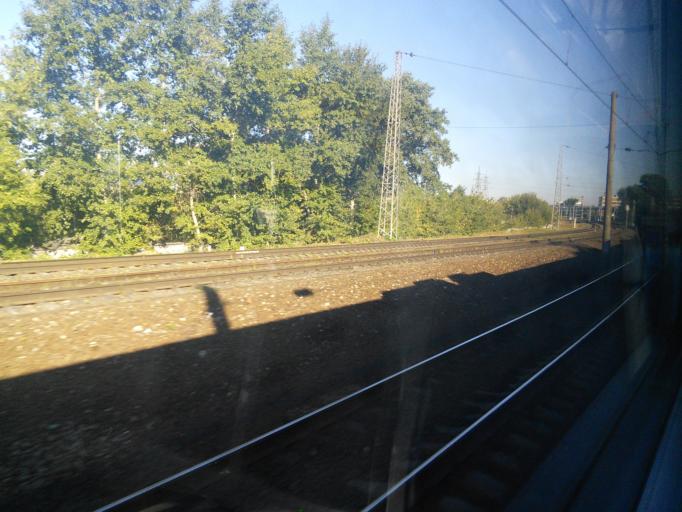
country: RU
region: Moscow
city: Tekstil'shchiki
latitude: 55.7113
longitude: 37.7288
